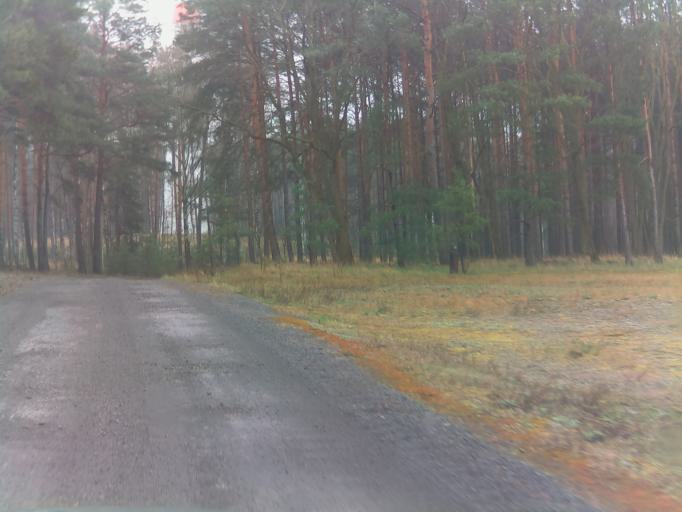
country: DE
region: Brandenburg
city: Jamlitz
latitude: 52.0576
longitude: 14.3573
